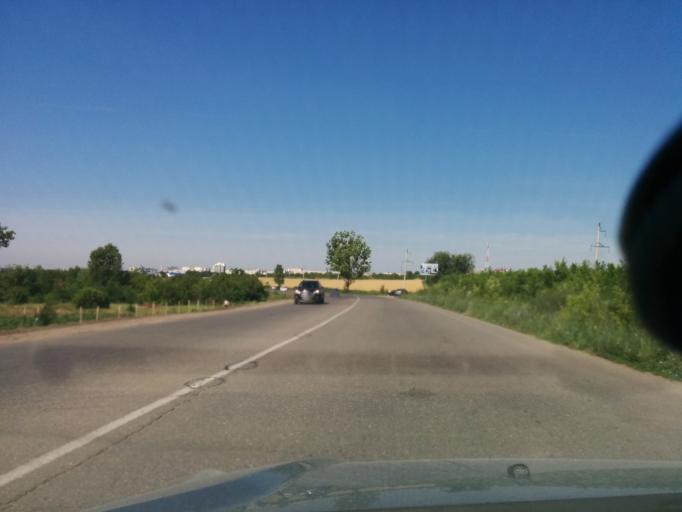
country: MD
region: Chisinau
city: Stauceni
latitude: 47.0484
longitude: 28.9171
